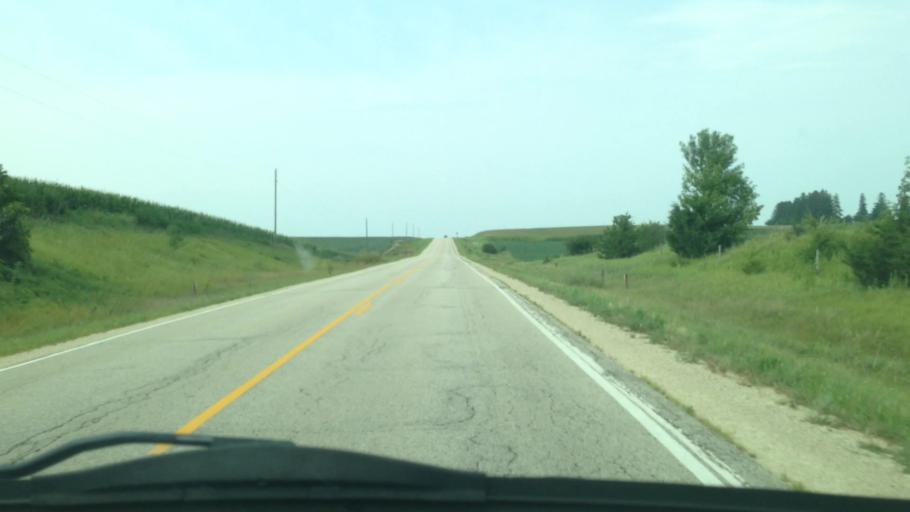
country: US
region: Minnesota
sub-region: Winona County
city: Saint Charles
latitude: 43.8560
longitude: -91.9593
